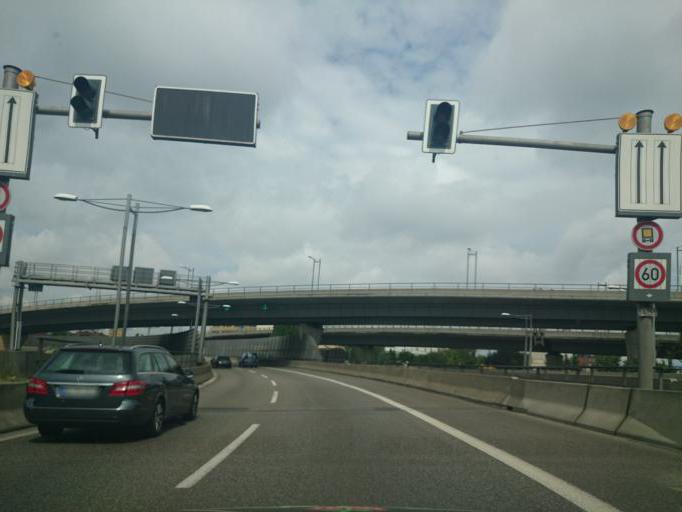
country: DE
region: Berlin
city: Treptow Bezirk
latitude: 52.4634
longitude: 13.4542
